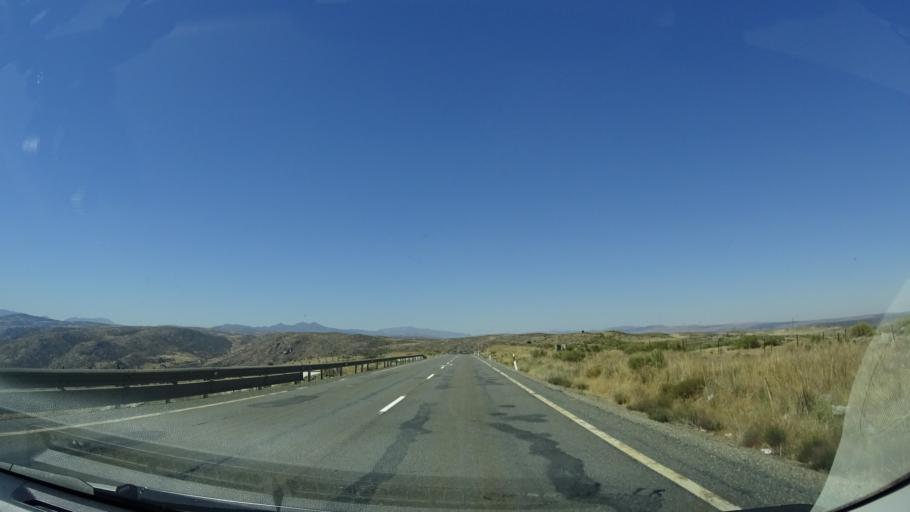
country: ES
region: Castille and Leon
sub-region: Provincia de Avila
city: Tornadizos de Avila
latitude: 40.6073
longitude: -4.5419
